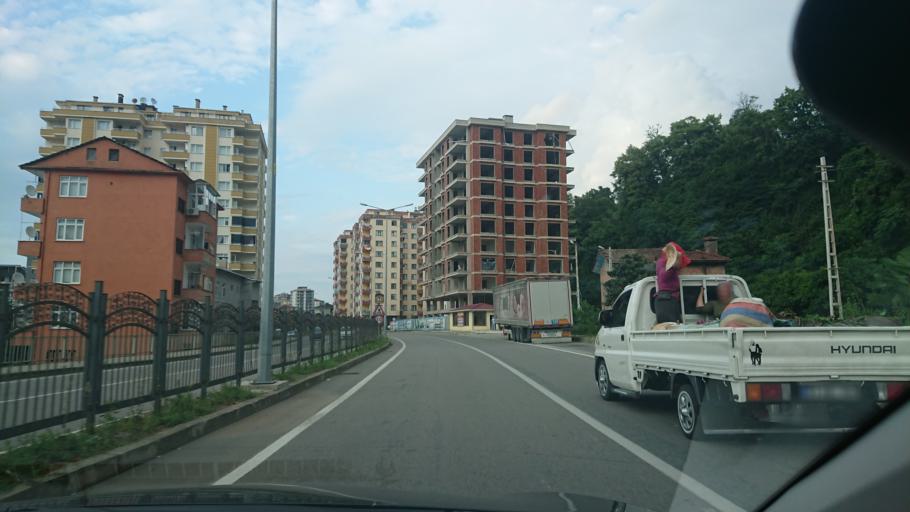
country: TR
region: Rize
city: Gundogdu
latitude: 41.0320
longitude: 40.5606
